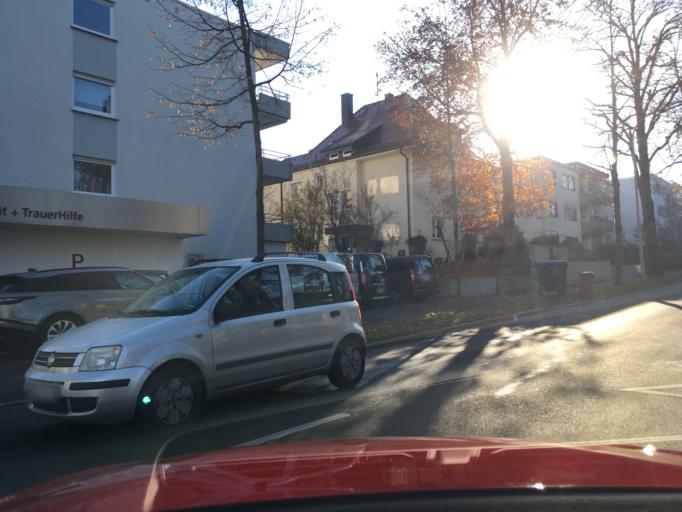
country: DE
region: Baden-Wuerttemberg
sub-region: Regierungsbezirk Stuttgart
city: Heilbronn
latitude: 49.1384
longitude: 9.2338
